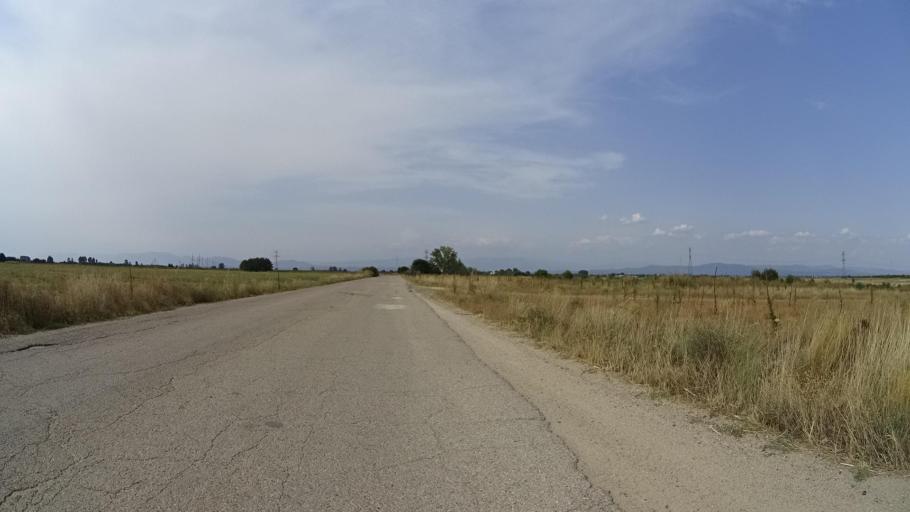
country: BG
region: Plovdiv
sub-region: Obshtina Kaloyanovo
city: Kaloyanovo
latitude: 42.3166
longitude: 24.7993
